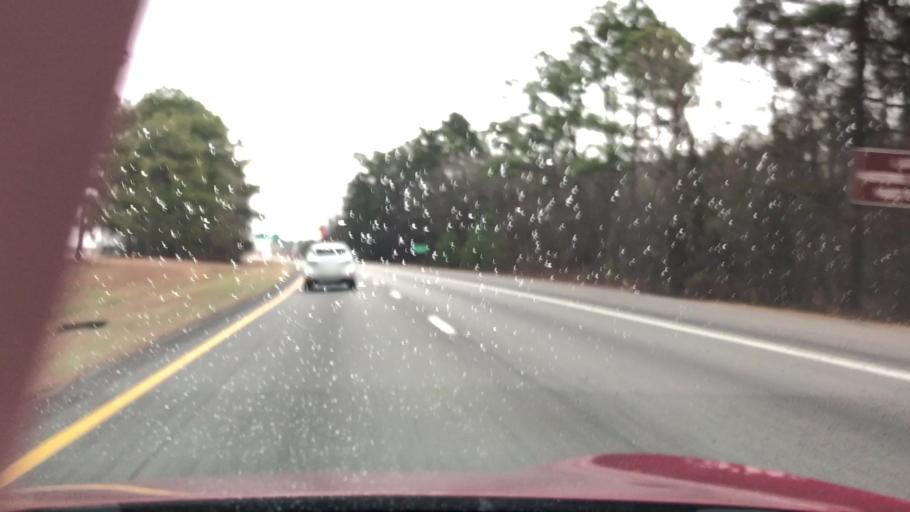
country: US
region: South Carolina
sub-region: Dillon County
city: Latta
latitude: 34.3391
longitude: -79.5403
